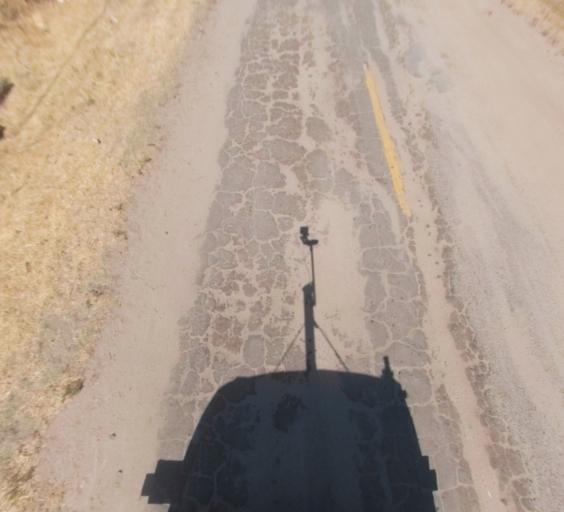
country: US
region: California
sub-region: Madera County
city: Parksdale
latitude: 36.9780
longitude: -120.0238
